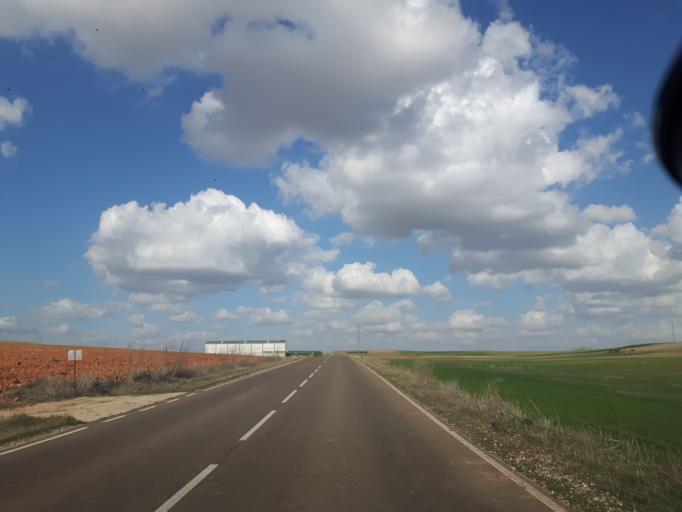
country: ES
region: Castille and Leon
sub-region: Provincia de Salamanca
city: Cabrerizos
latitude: 40.9927
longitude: -5.5962
